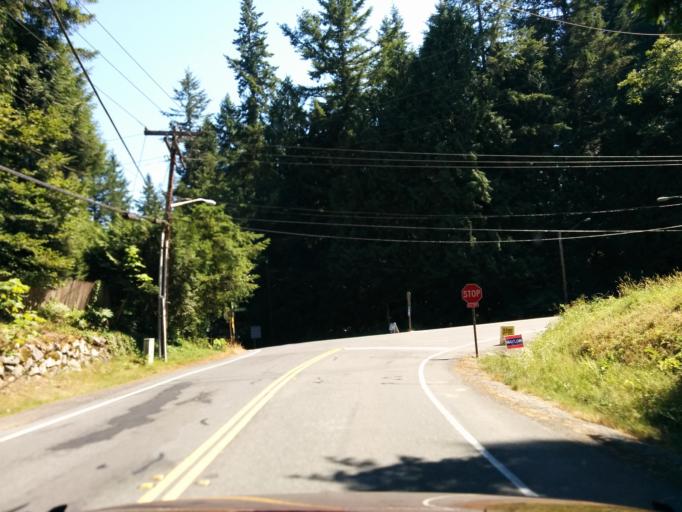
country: US
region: Washington
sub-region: King County
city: Union Hill-Novelty Hill
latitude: 47.6667
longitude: -122.0224
